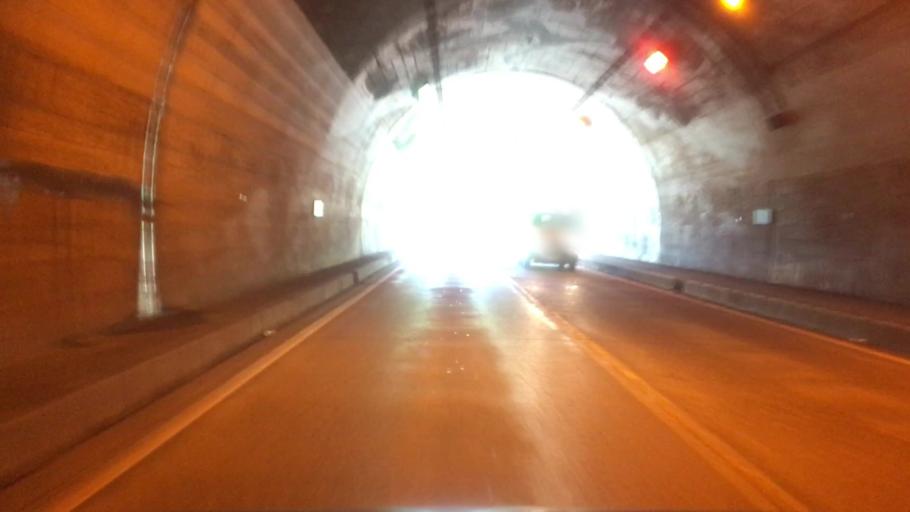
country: JP
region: Hyogo
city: Toyooka
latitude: 35.5835
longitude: 134.7417
